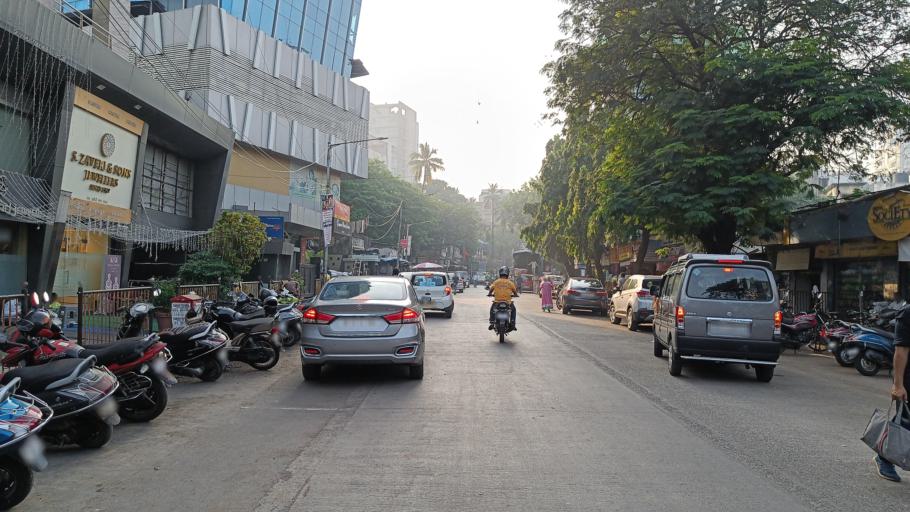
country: IN
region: Maharashtra
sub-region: Mumbai Suburban
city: Mumbai
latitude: 19.0701
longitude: 72.8387
